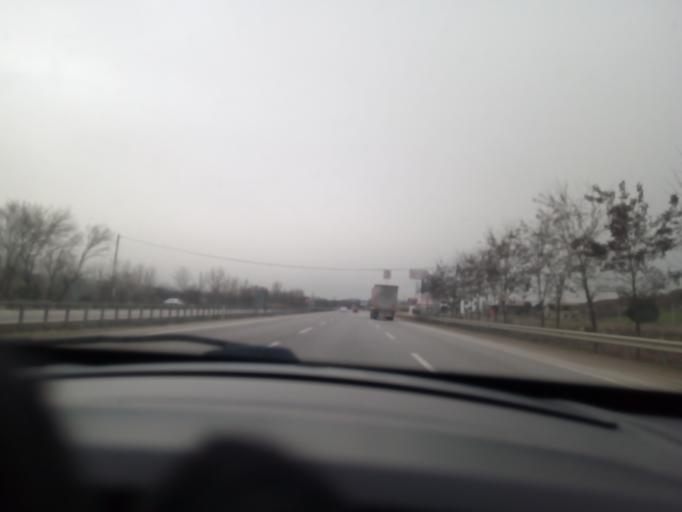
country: TR
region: Balikesir
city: Susurluk
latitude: 39.9677
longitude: 28.1714
